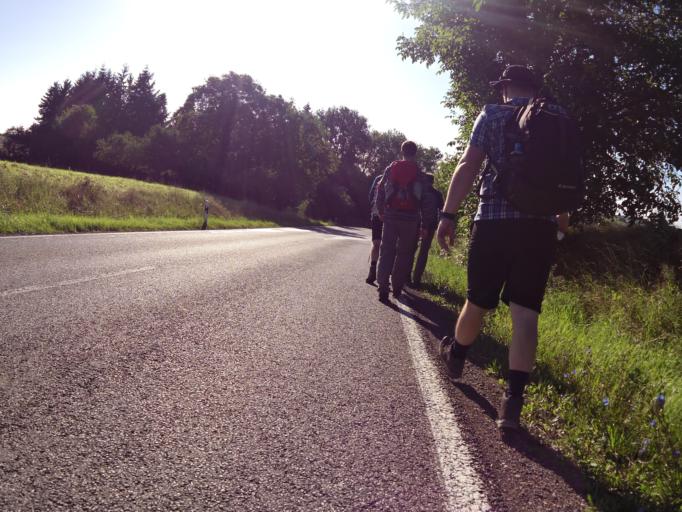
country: DE
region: Rheinland-Pfalz
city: Waldbockelheim
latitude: 49.8207
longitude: 7.7098
